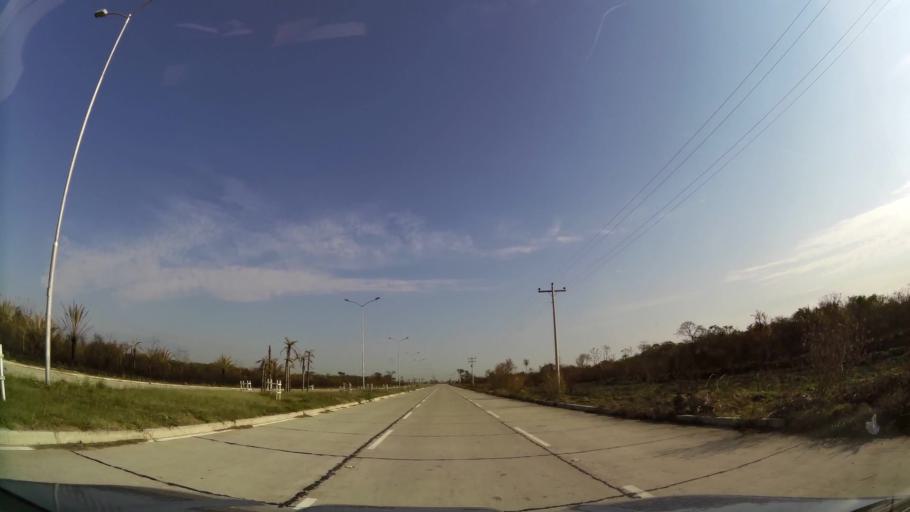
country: BO
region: Santa Cruz
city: Santa Cruz de la Sierra
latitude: -17.6729
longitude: -63.1263
